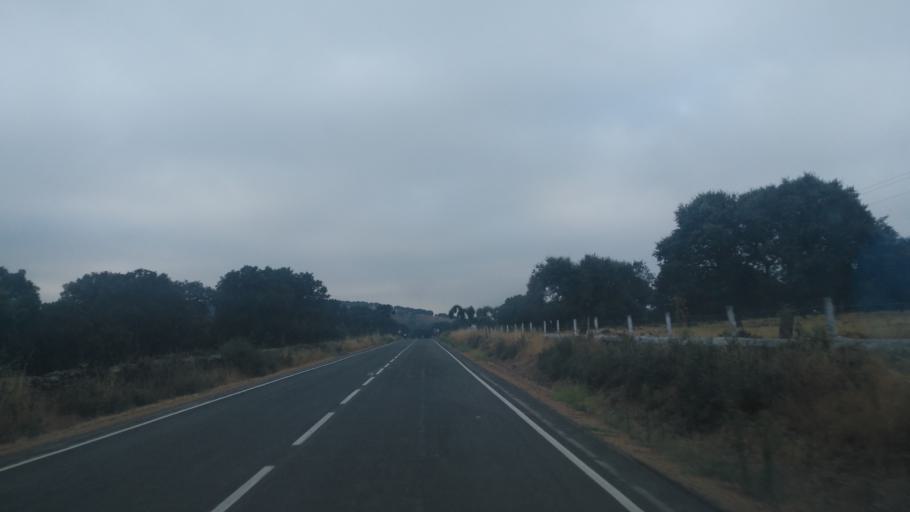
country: ES
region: Castille and Leon
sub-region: Provincia de Salamanca
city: Matilla de los Canos del Rio
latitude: 40.8077
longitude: -5.9274
